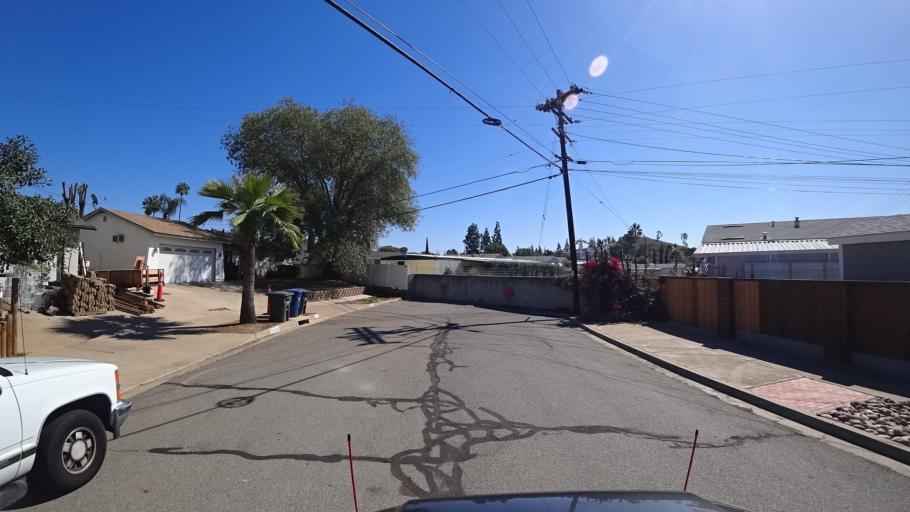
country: US
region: California
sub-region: San Diego County
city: Bostonia
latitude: 32.8215
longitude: -116.9552
